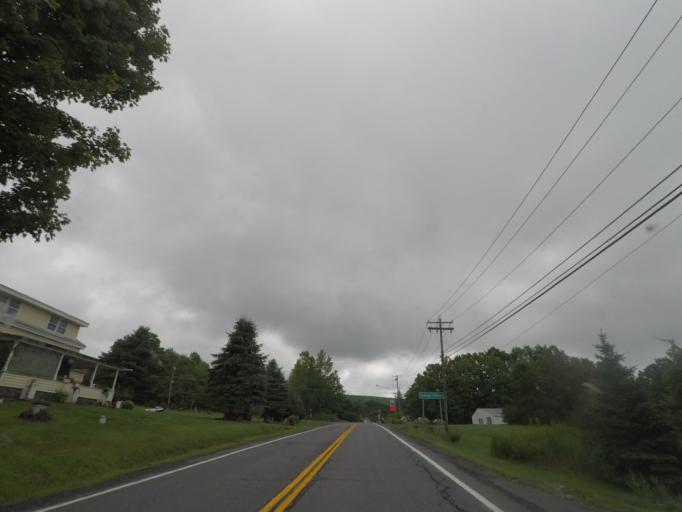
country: US
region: New York
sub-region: Rensselaer County
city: Averill Park
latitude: 42.5872
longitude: -73.4884
